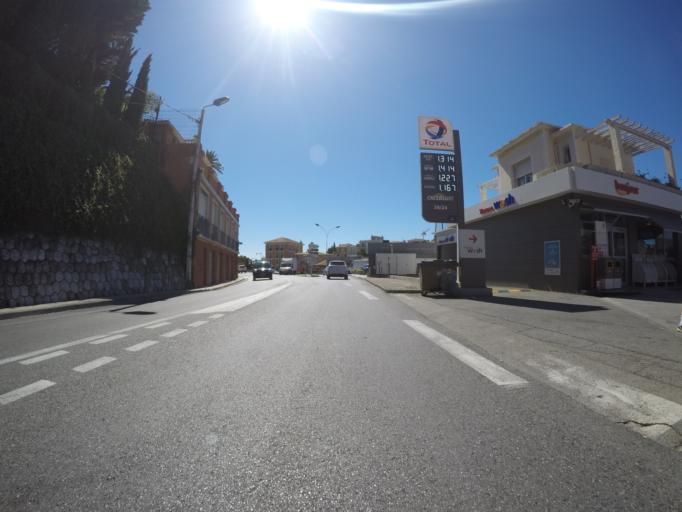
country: FR
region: Provence-Alpes-Cote d'Azur
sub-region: Departement des Alpes-Maritimes
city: Beaulieu-sur-Mer
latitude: 43.7022
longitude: 7.3252
